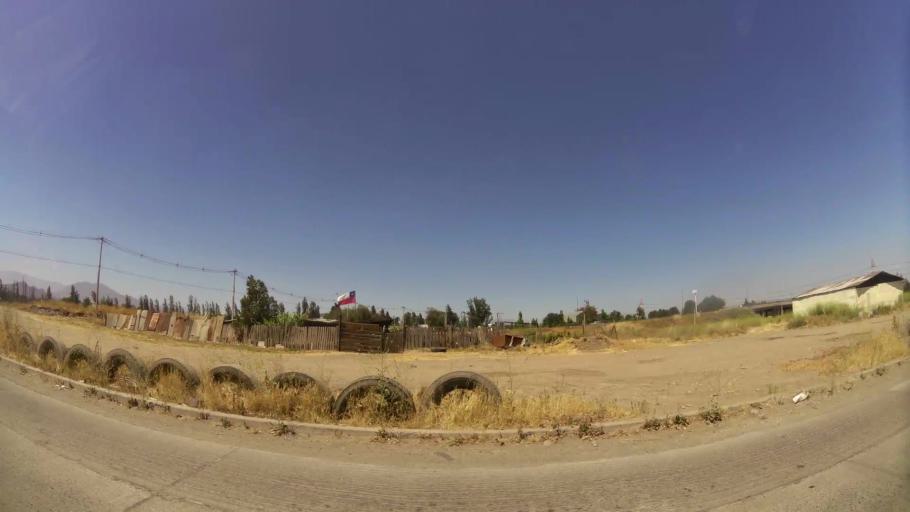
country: CL
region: Santiago Metropolitan
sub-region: Provincia de Maipo
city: San Bernardo
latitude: -33.6260
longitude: -70.7124
